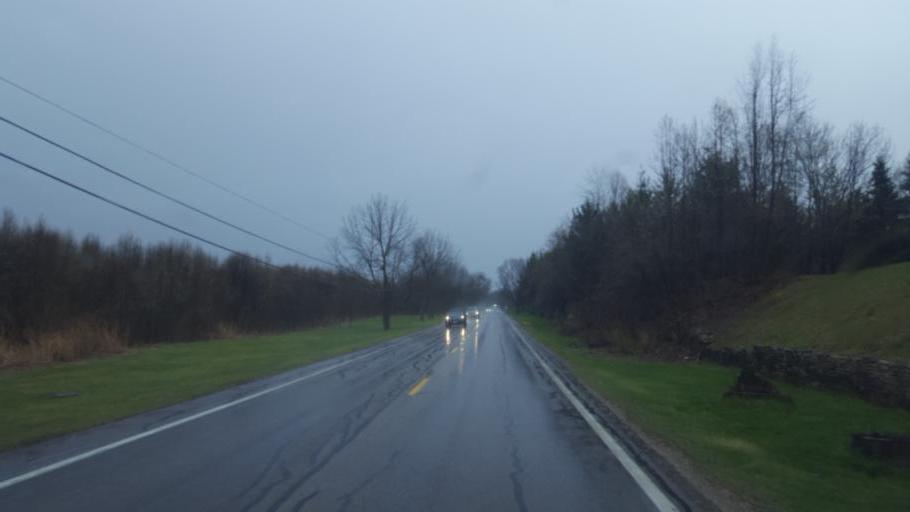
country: US
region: Ohio
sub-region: Delaware County
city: Powell
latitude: 40.1433
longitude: -83.0405
